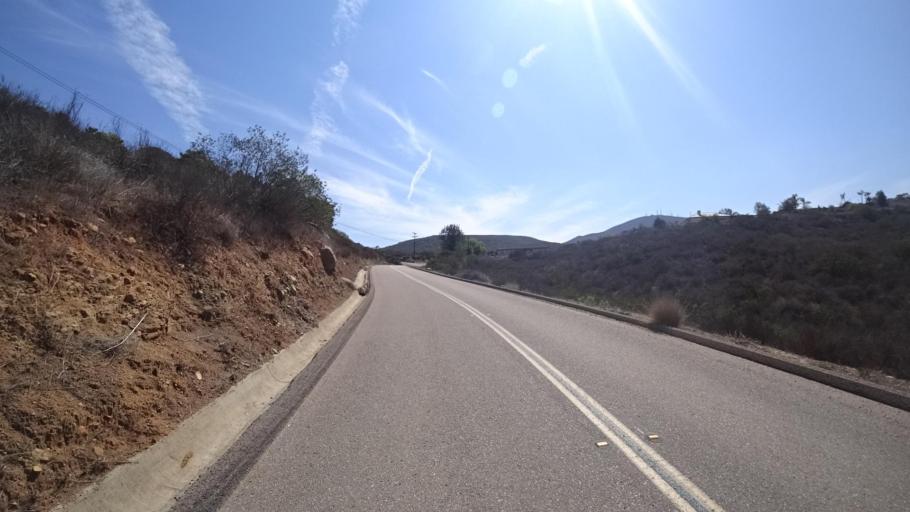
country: US
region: California
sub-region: San Diego County
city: Rancho San Diego
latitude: 32.7193
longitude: -116.9285
